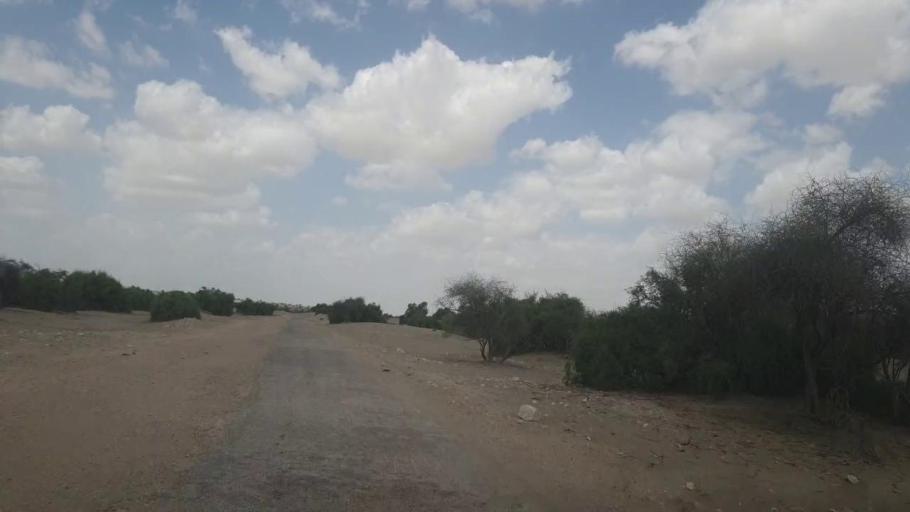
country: PK
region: Sindh
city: Kot Diji
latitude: 27.2772
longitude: 69.2216
